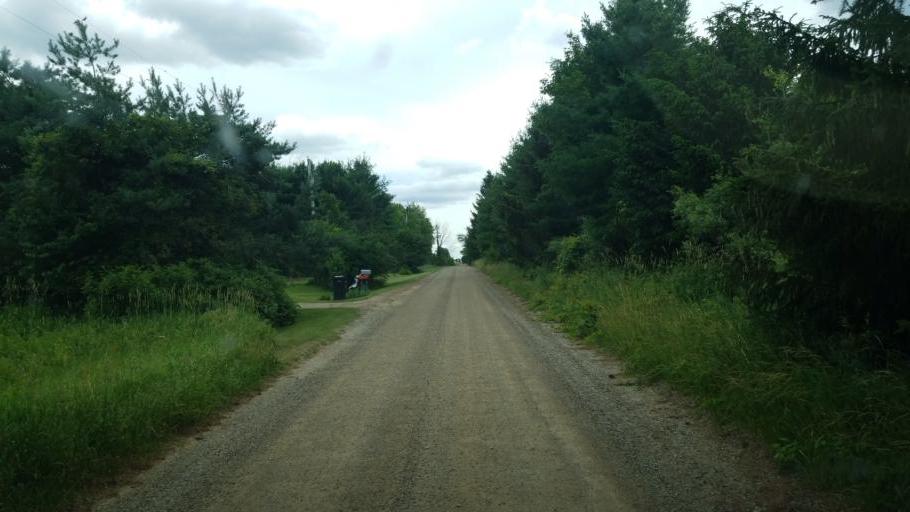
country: US
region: Michigan
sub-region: Barry County
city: Nashville
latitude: 42.6896
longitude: -84.9756
